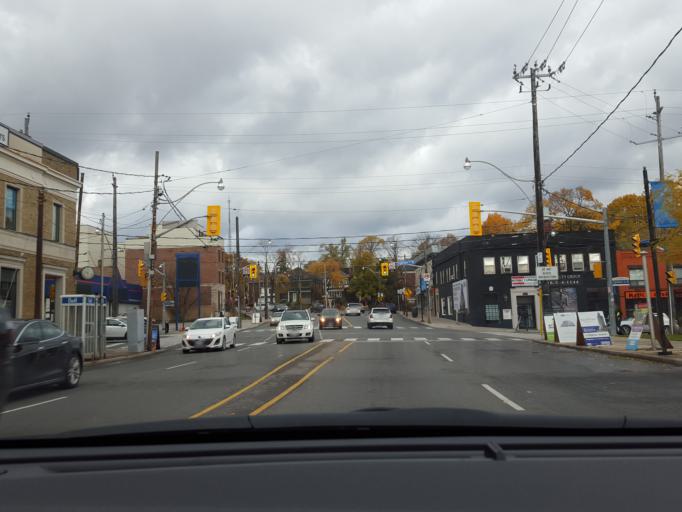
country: CA
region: Ontario
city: Toronto
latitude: 43.7042
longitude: -79.4083
